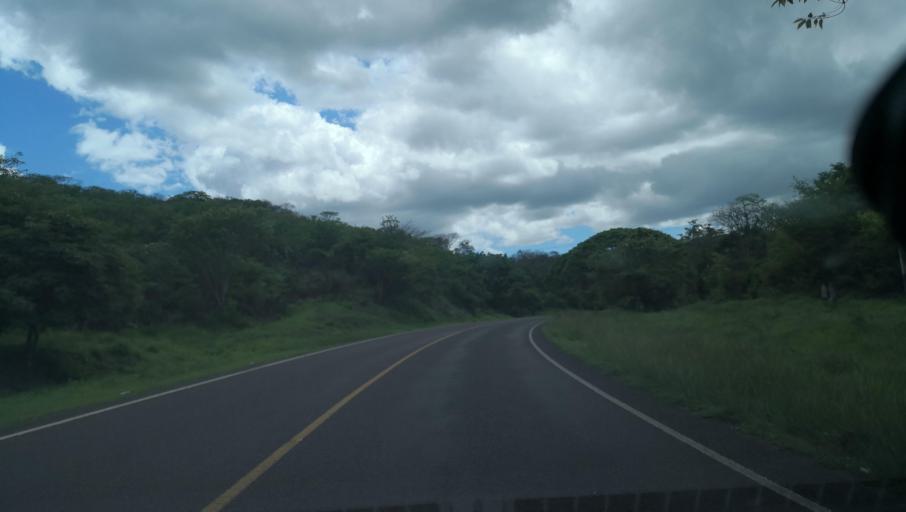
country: NI
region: Madriz
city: Palacaguina
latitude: 13.4338
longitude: -86.4265
